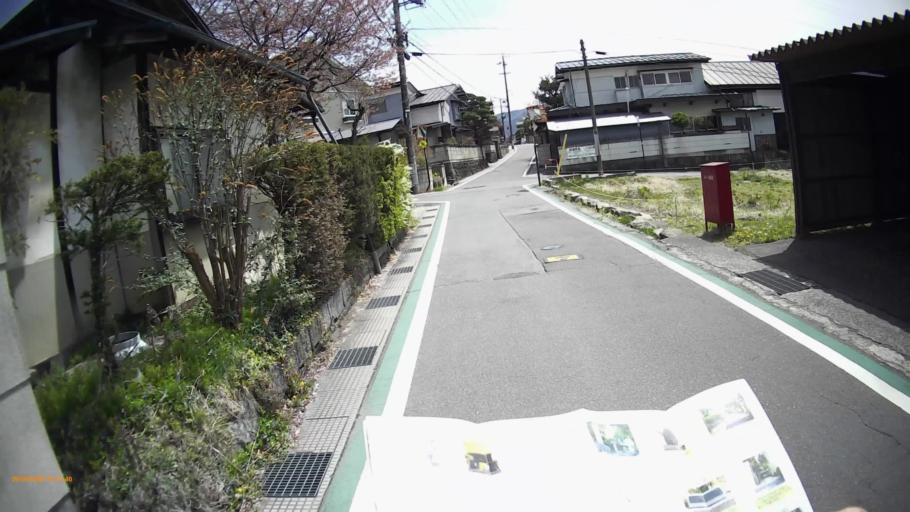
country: JP
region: Nagano
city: Chino
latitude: 36.0149
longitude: 138.1391
